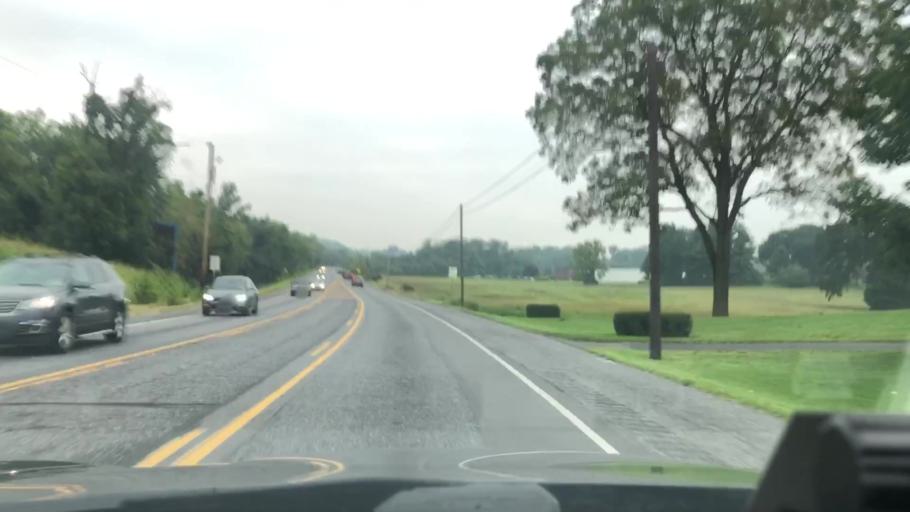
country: US
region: Pennsylvania
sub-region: Berks County
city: Blandon
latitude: 40.4441
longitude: -75.9046
